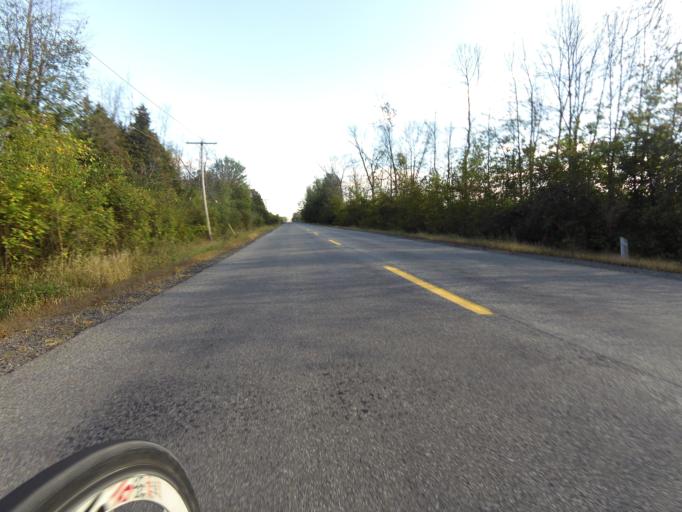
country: CA
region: Ontario
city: Bells Corners
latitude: 45.1275
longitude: -75.7454
